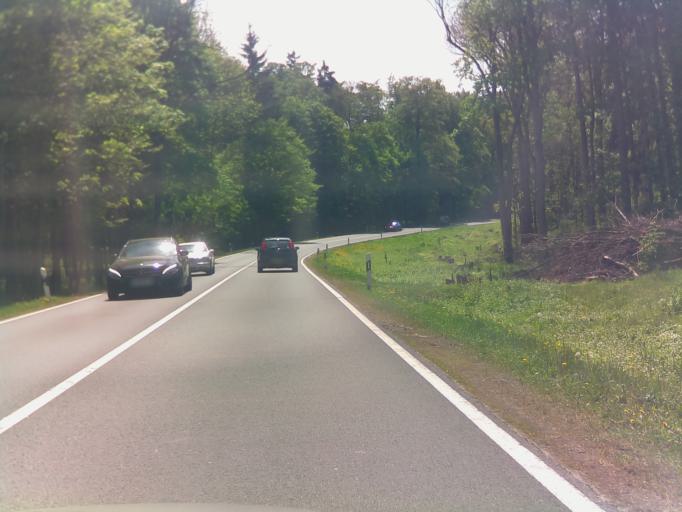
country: DE
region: Saxony-Anhalt
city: Hasselfelde
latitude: 51.7151
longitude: 10.8928
